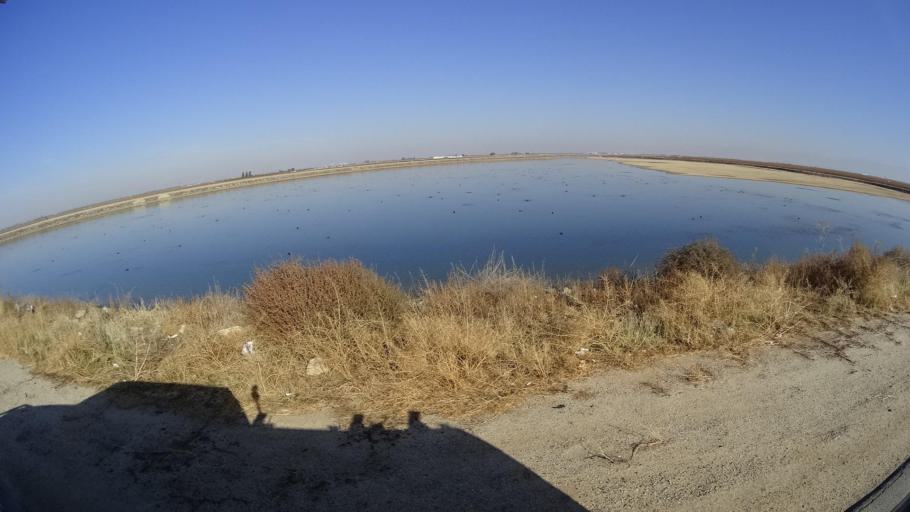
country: US
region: California
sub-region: Kern County
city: Delano
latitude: 35.7471
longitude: -119.1795
